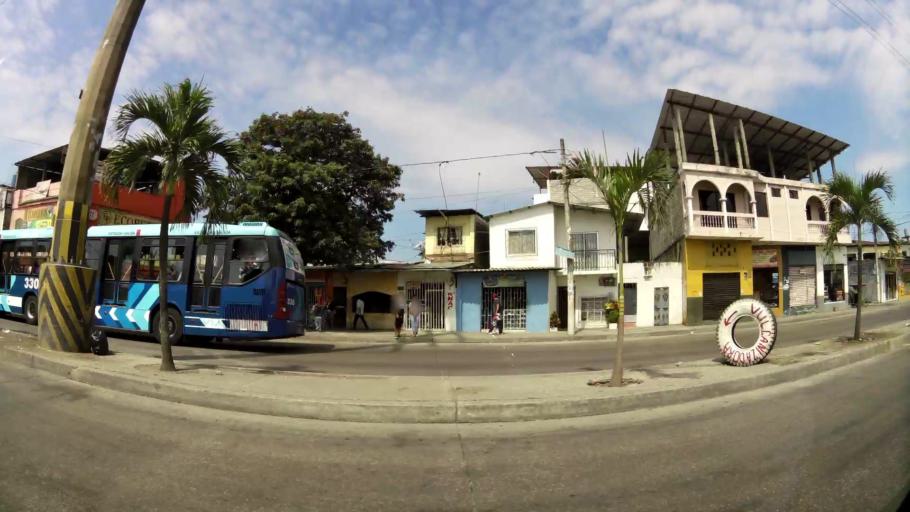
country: EC
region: Guayas
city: Guayaquil
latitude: -2.2583
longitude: -79.8910
